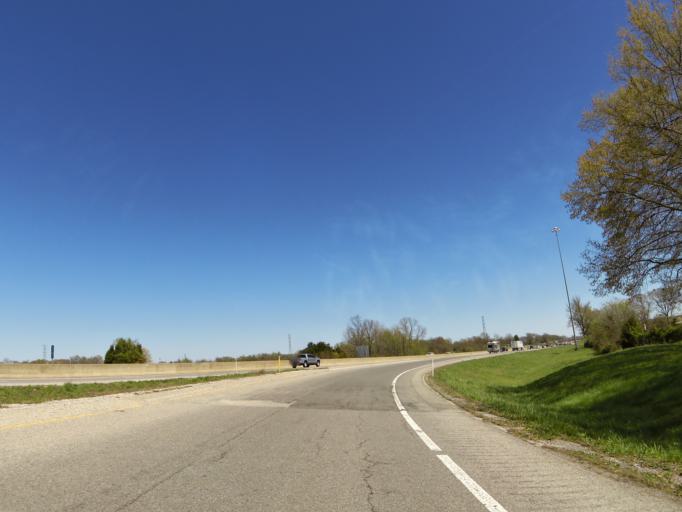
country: US
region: Kentucky
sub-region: Warren County
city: Bowling Green
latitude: 37.0072
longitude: -86.3634
